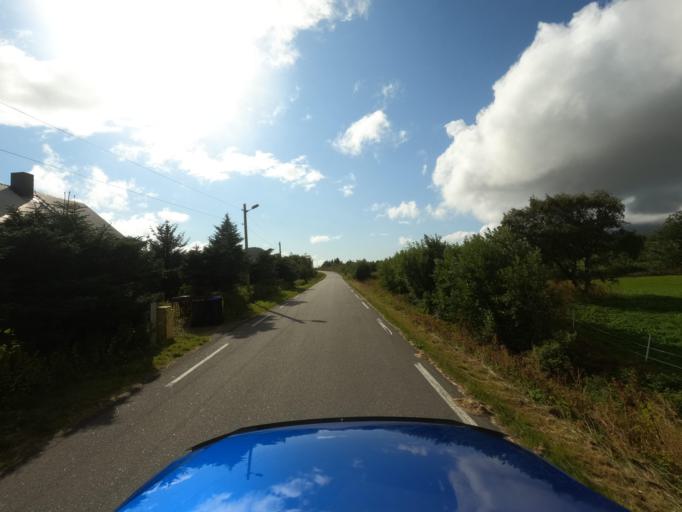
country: NO
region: Nordland
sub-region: Vagan
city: Kabelvag
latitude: 68.2381
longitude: 14.1160
